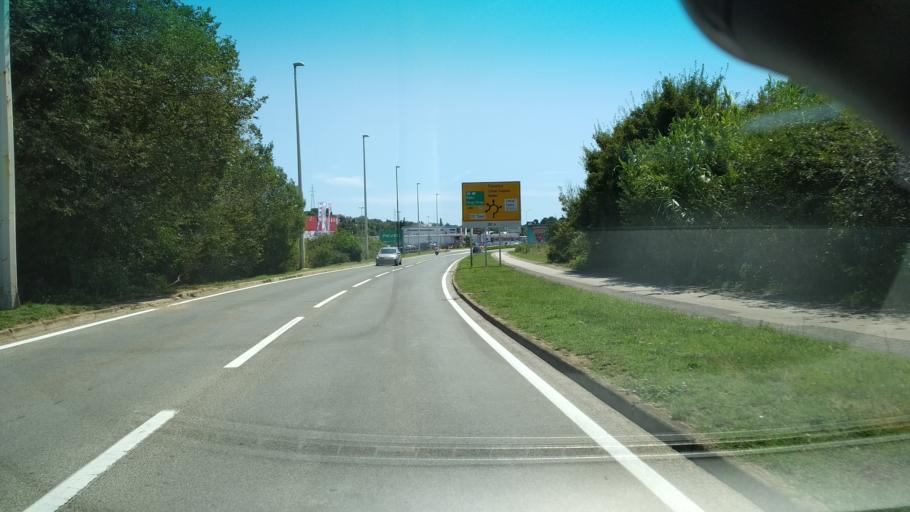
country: HR
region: Istarska
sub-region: Grad Pula
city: Pula
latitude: 44.8849
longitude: 13.8601
